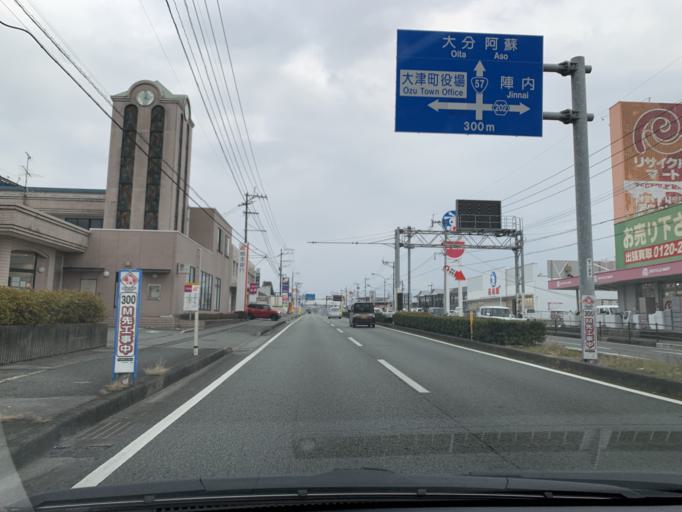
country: JP
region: Kumamoto
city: Ozu
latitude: 32.8756
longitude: 130.8670
